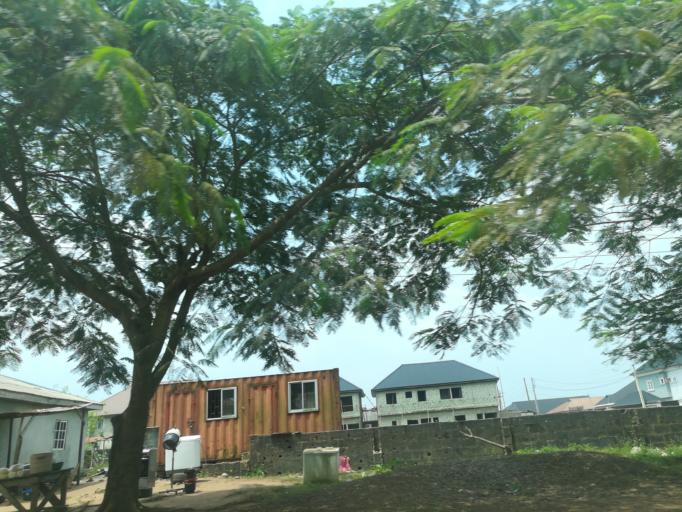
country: NG
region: Lagos
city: Ikorodu
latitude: 6.6057
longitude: 3.5984
